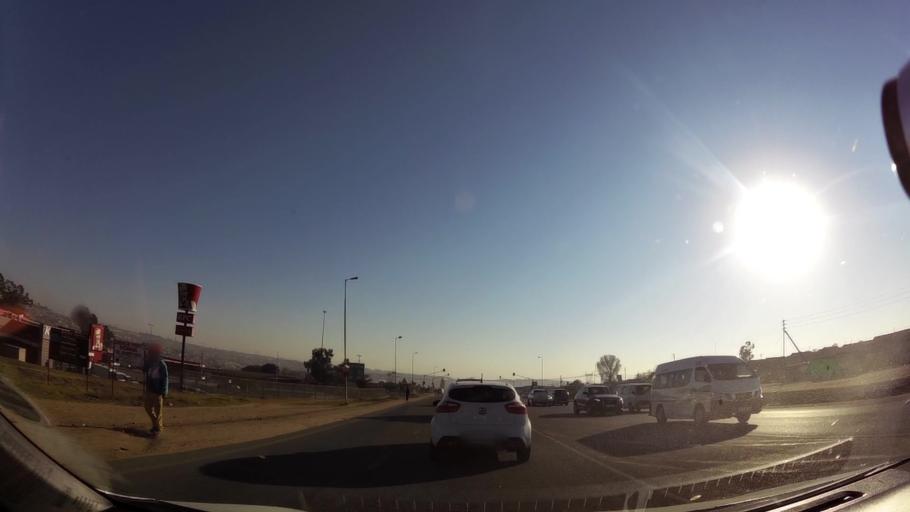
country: ZA
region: Gauteng
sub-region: City of Johannesburg Metropolitan Municipality
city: Midrand
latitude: -25.9245
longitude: 28.0983
